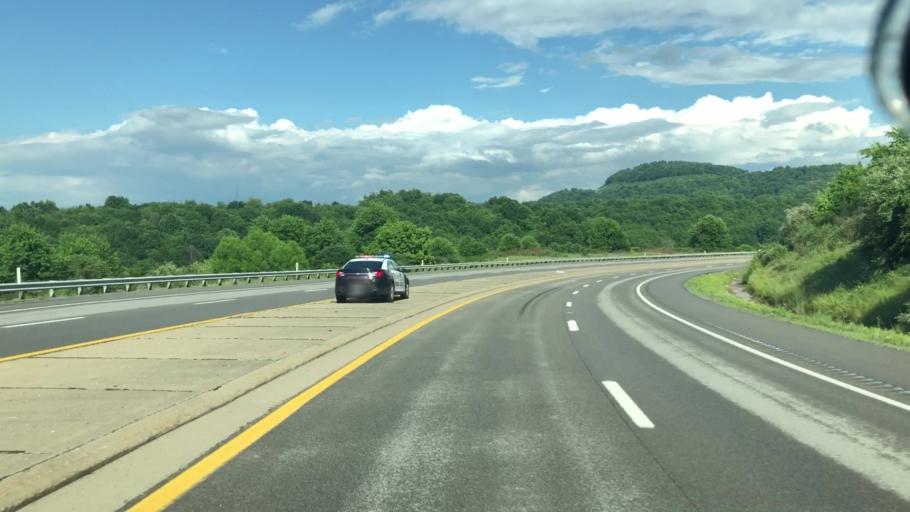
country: US
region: West Virginia
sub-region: Harrison County
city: Bridgeport
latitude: 39.3034
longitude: -80.2096
